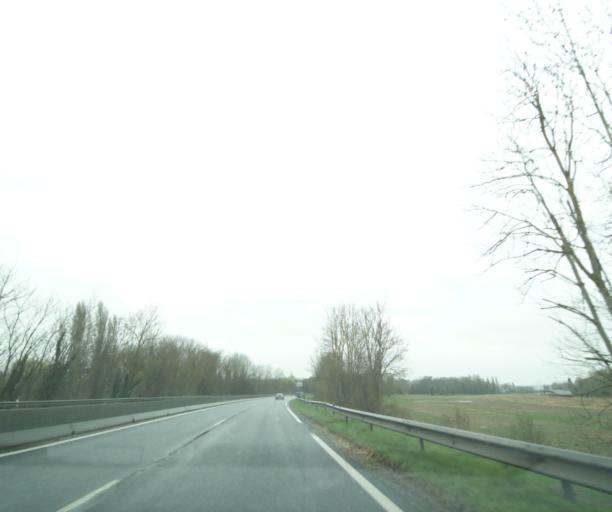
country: FR
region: Ile-de-France
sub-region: Departement de l'Essonne
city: Morigny-Champigny
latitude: 48.4461
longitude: 2.1757
